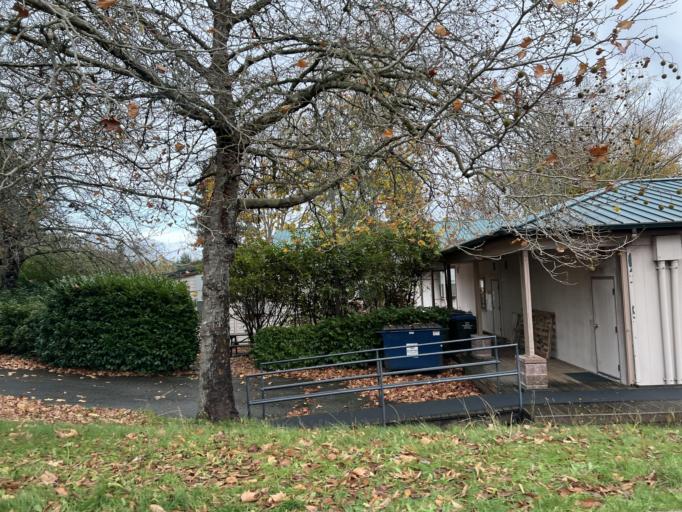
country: US
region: Washington
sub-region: Kitsap County
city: Bainbridge Island
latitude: 47.6389
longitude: -122.5222
